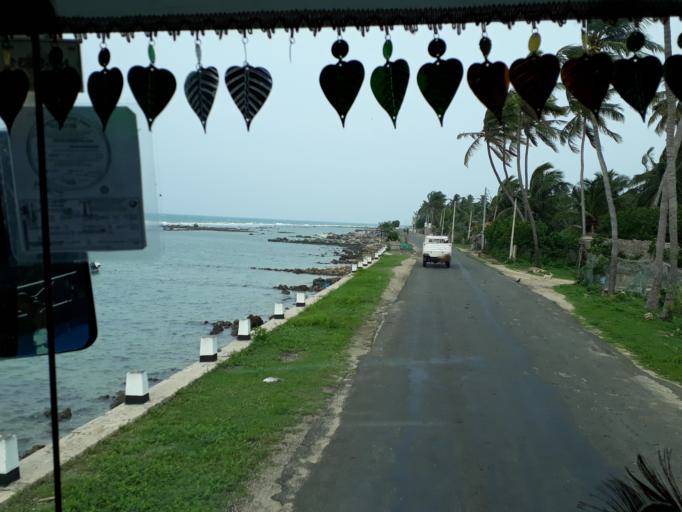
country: LK
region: Northern Province
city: Point Pedro
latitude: 9.8327
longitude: 80.2033
